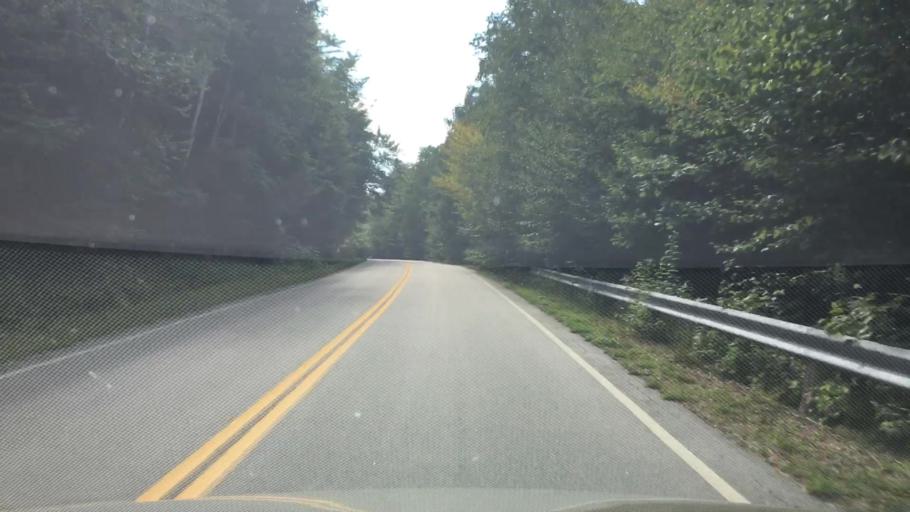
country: US
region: New Hampshire
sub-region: Carroll County
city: North Conway
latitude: 44.0453
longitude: -71.3103
